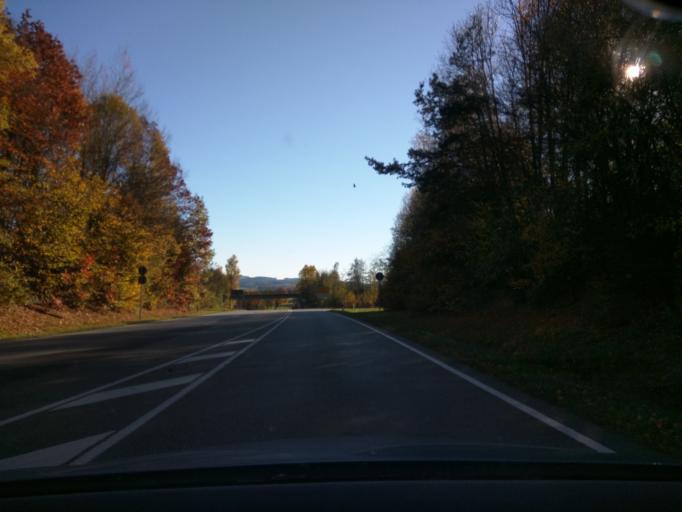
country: DE
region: Bavaria
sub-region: Lower Bavaria
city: Salzweg
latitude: 48.5988
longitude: 13.4765
